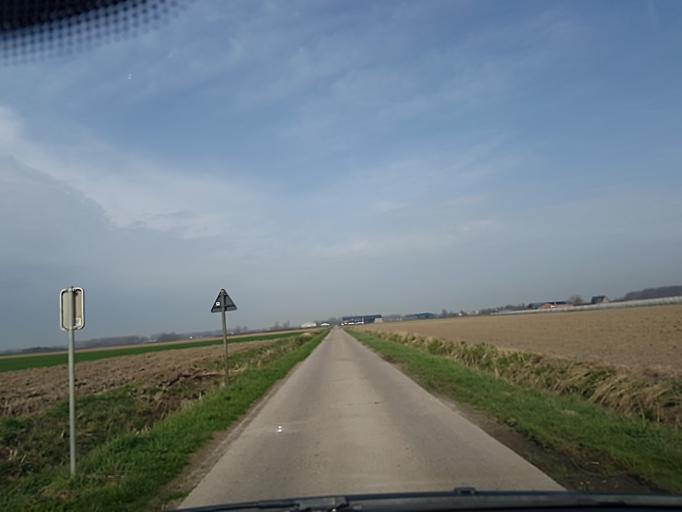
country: BE
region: Flanders
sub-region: Provincie Oost-Vlaanderen
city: Sint-Gillis-Waas
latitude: 51.2677
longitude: 4.1808
